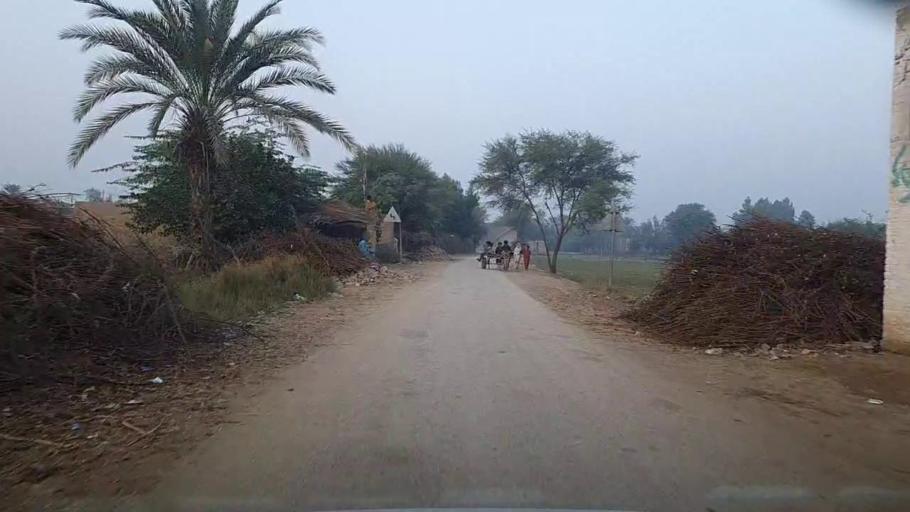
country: PK
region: Sindh
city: Bozdar
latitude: 27.0666
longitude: 68.5971
